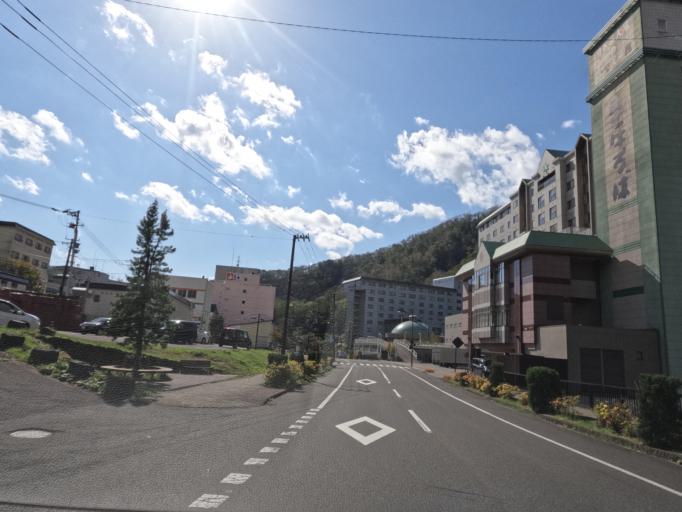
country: JP
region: Hokkaido
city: Shiraoi
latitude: 42.4939
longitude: 141.1426
